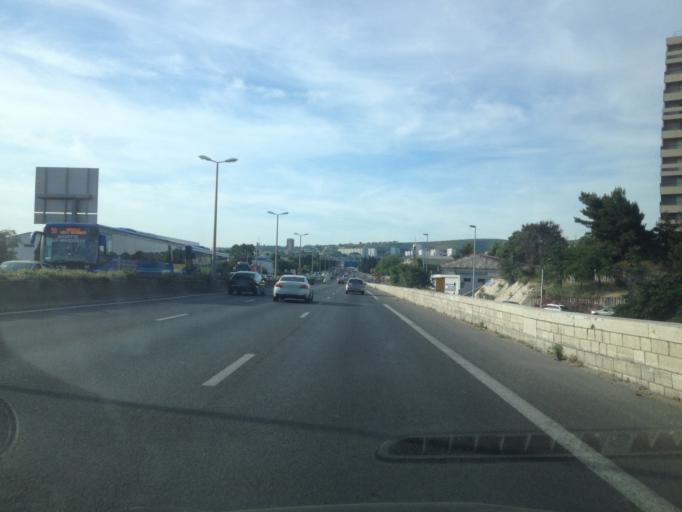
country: FR
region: Provence-Alpes-Cote d'Azur
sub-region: Departement des Bouches-du-Rhone
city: Marseille 14
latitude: 43.3315
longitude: 5.3778
